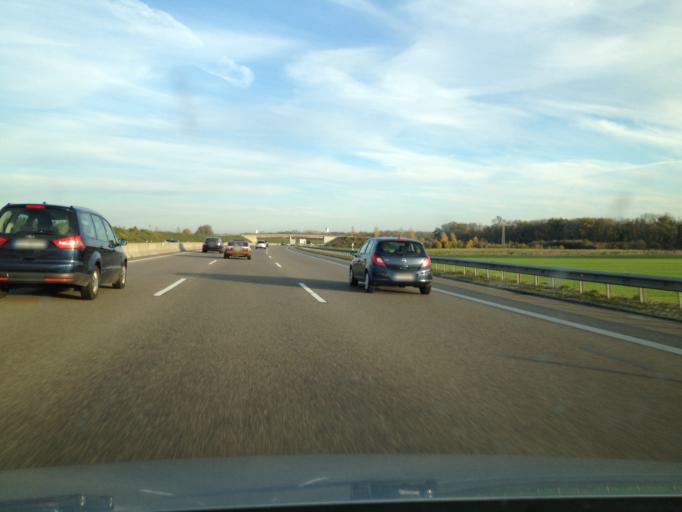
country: DE
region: Bavaria
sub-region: Swabia
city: Leipheim
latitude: 48.4579
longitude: 10.1855
